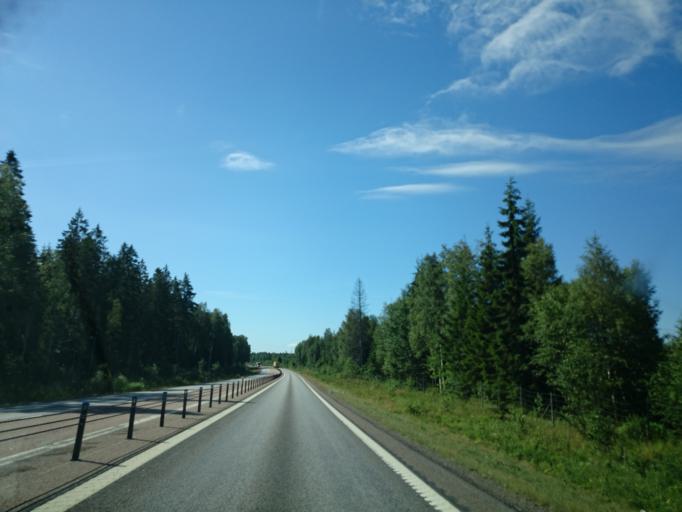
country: SE
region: Gaevleborg
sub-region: Soderhamns Kommun
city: Ljusne
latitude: 61.1892
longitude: 17.0462
